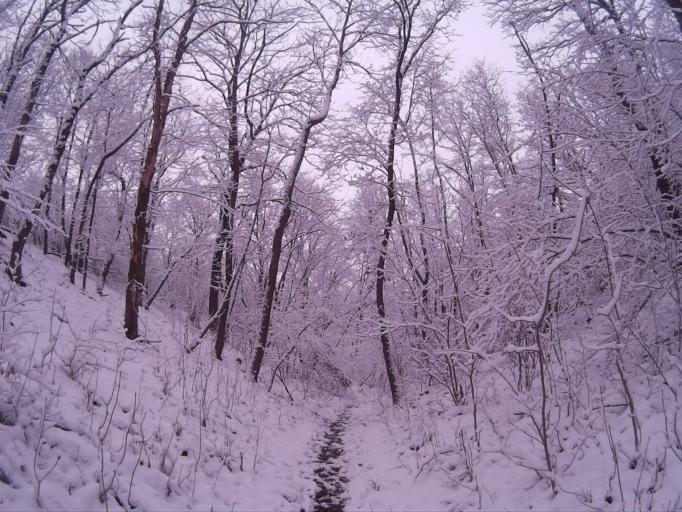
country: HU
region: Fejer
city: Szarliget
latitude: 47.5195
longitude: 18.5025
